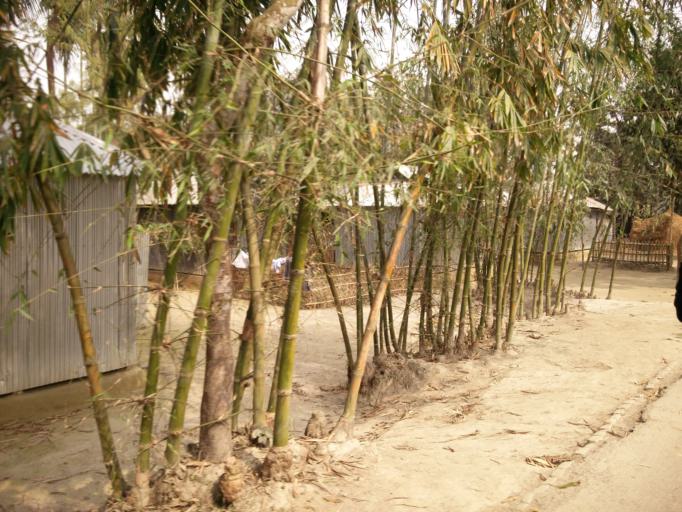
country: BD
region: Rangpur Division
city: Nageswari
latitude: 25.8817
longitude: 89.6905
